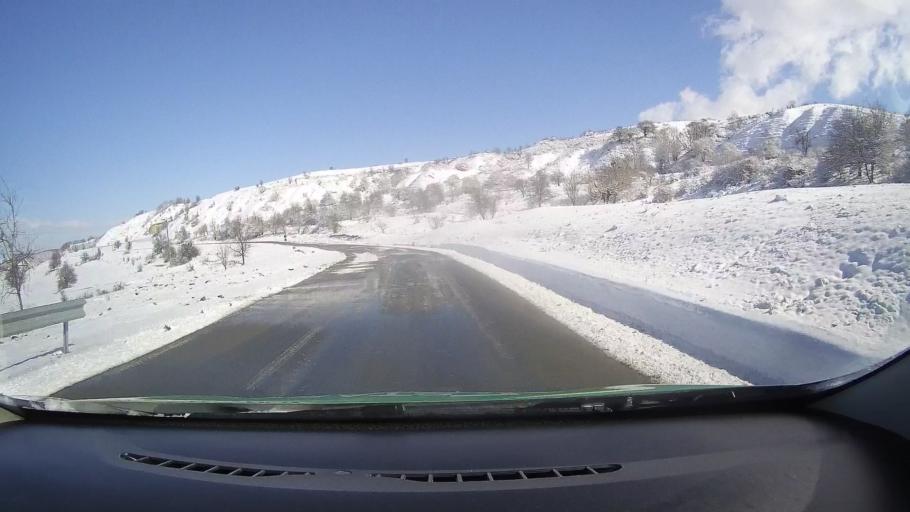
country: RO
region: Sibiu
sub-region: Comuna Avrig
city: Avrig
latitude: 45.7812
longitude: 24.3733
